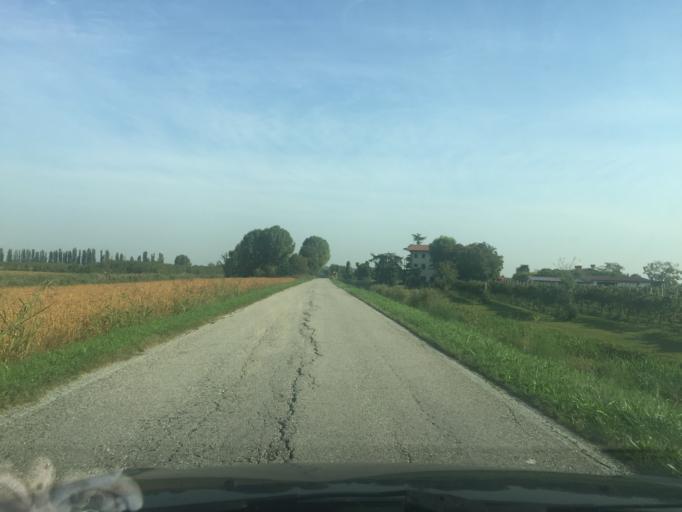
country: IT
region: Veneto
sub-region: Provincia di Venezia
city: Passarella
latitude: 45.6265
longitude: 12.6472
